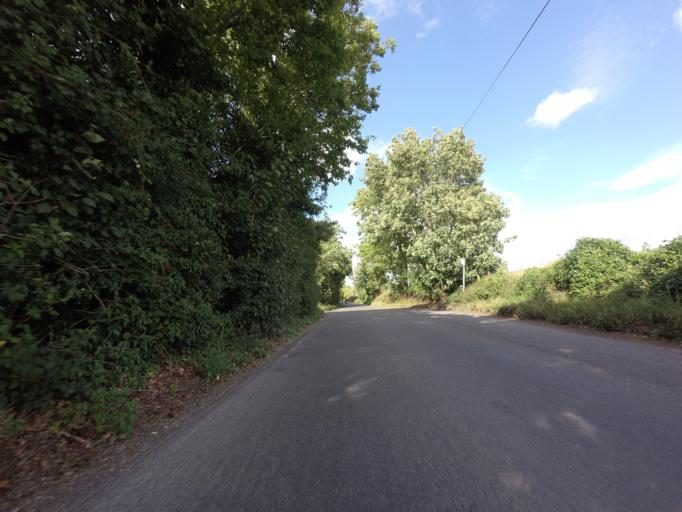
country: GB
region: England
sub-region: Kent
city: Eynsford
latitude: 51.3819
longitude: 0.2371
